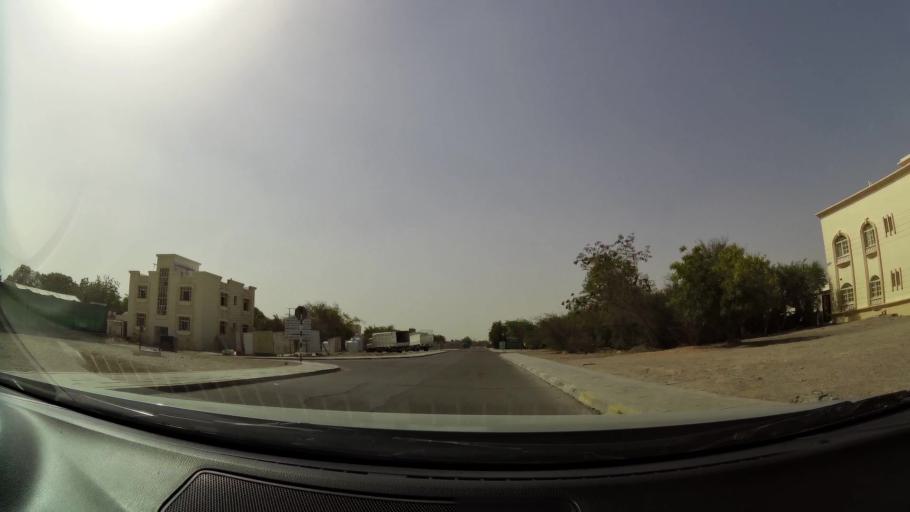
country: AE
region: Abu Dhabi
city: Al Ain
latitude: 24.2312
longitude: 55.6980
